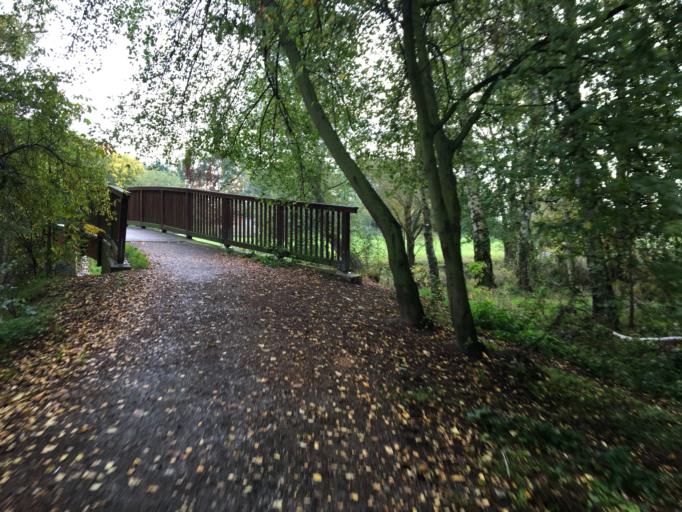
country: DE
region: Lower Saxony
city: Braunschweig
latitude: 52.2981
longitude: 10.5708
